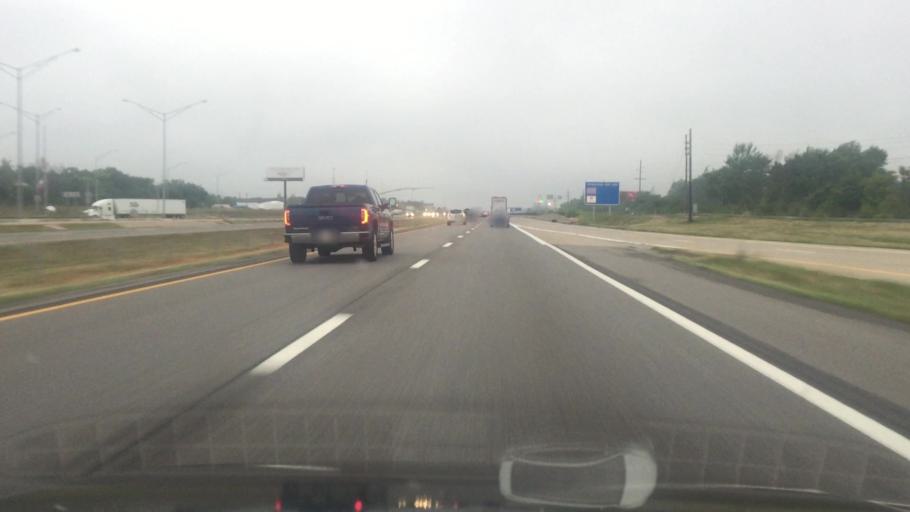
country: US
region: Missouri
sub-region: Warren County
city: Wright City
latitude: 38.8126
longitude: -90.9378
